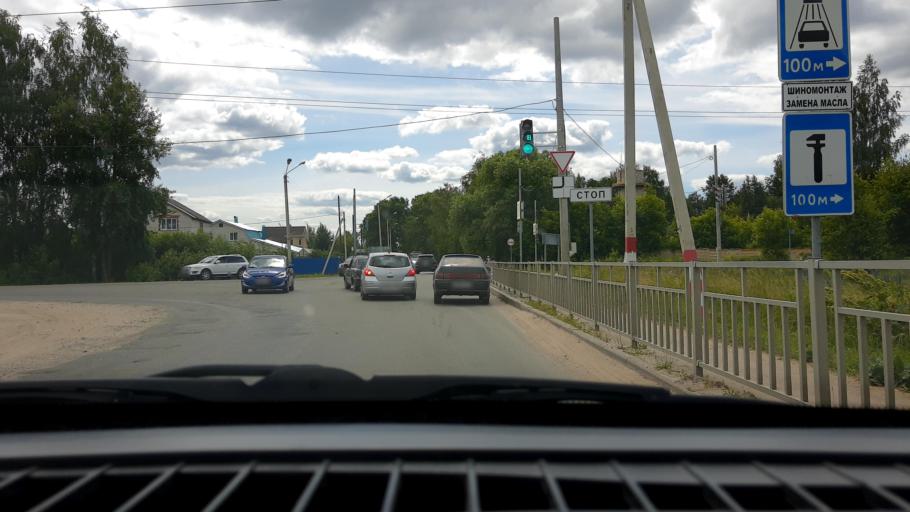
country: RU
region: Nizjnij Novgorod
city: Bor
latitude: 56.3825
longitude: 44.0365
